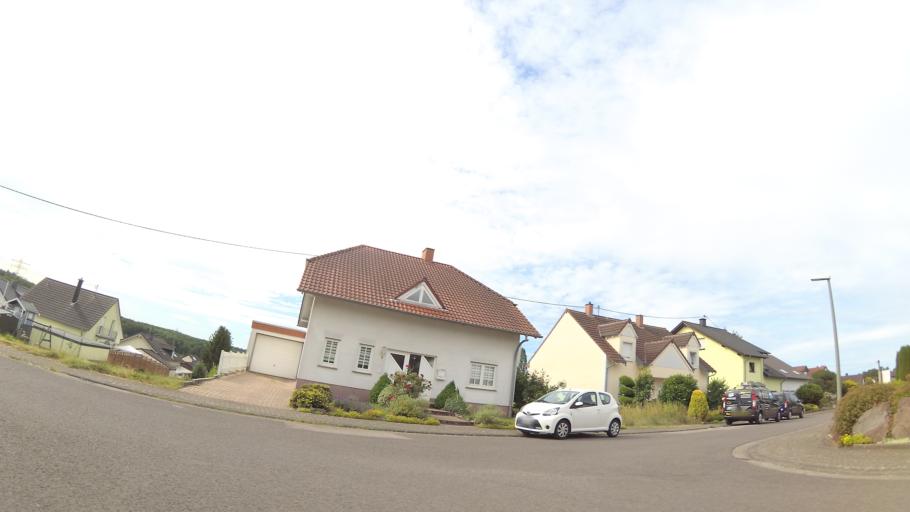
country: DE
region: Saarland
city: Schwalbach
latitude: 49.3246
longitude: 6.8198
